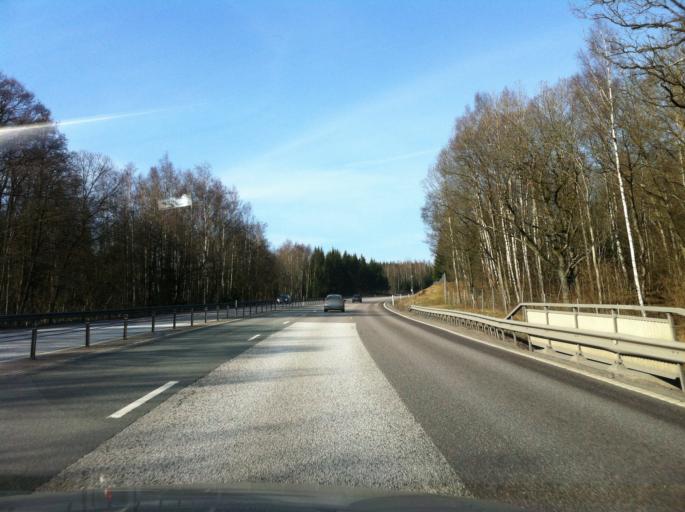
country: SE
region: Joenkoeping
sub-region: Jonkopings Kommun
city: Jonkoping
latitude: 57.7497
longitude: 14.1198
